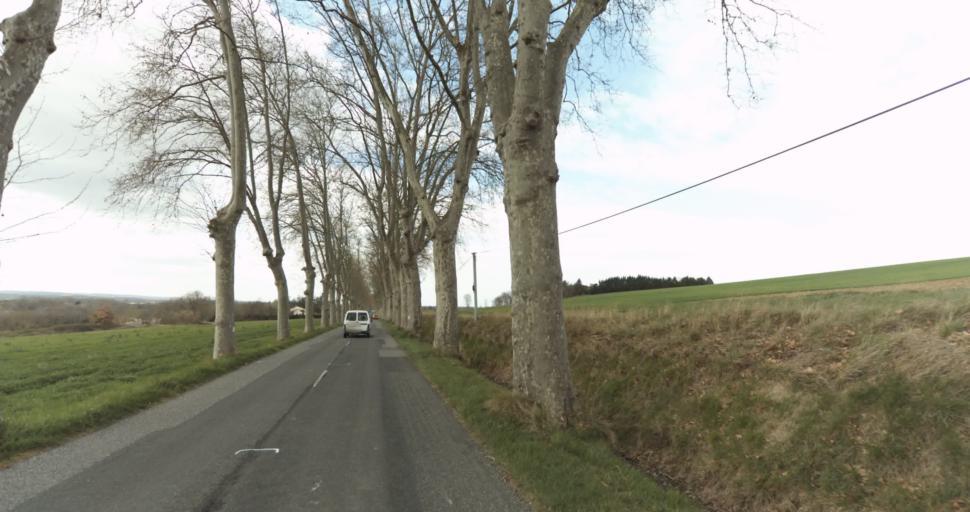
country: FR
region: Midi-Pyrenees
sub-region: Departement de la Haute-Garonne
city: Auterive
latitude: 43.3683
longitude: 1.4726
